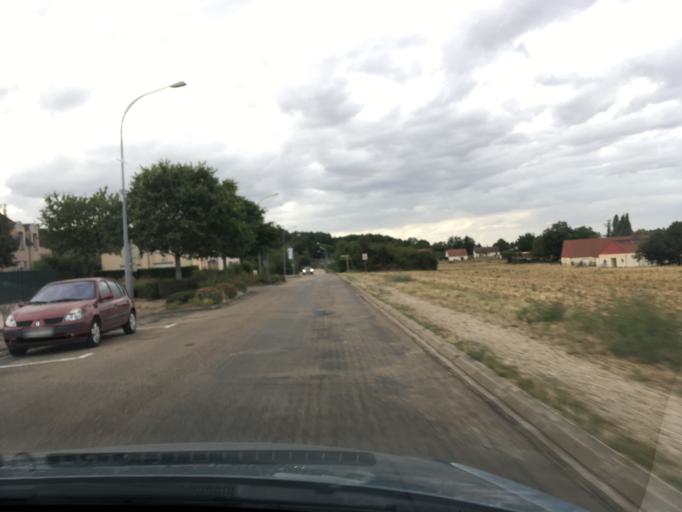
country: FR
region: Bourgogne
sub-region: Departement de l'Yonne
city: Appoigny
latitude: 47.8718
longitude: 3.5204
